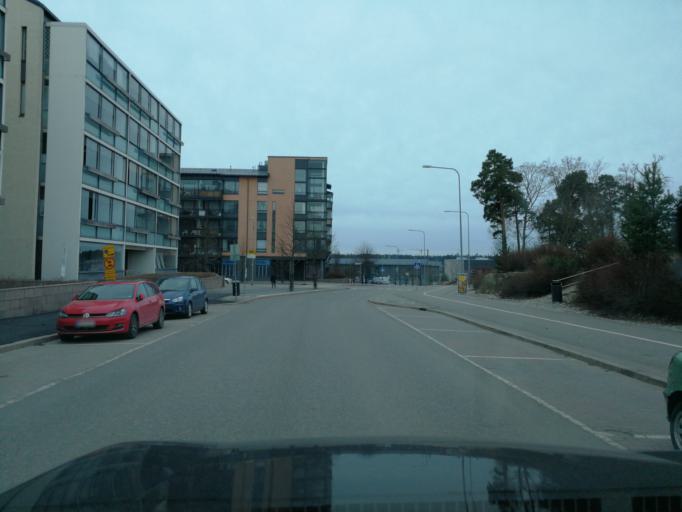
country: FI
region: Uusimaa
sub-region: Helsinki
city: Helsinki
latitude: 60.1909
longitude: 25.0253
